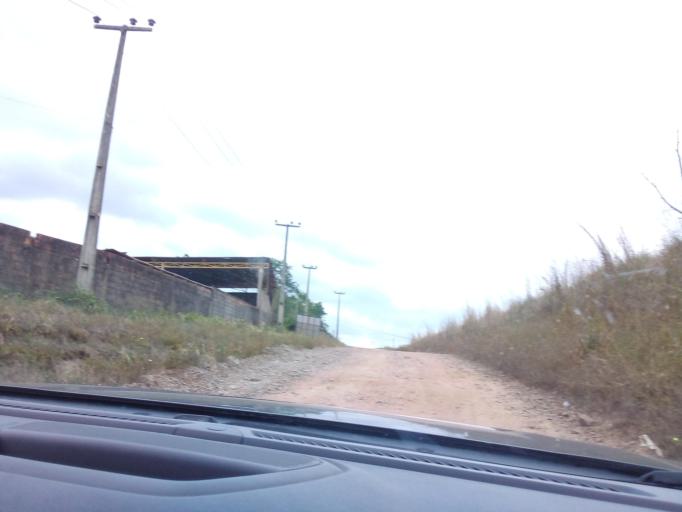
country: BR
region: Maranhao
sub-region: Sao Luis
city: Sao Luis
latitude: -2.6741
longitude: -44.2960
